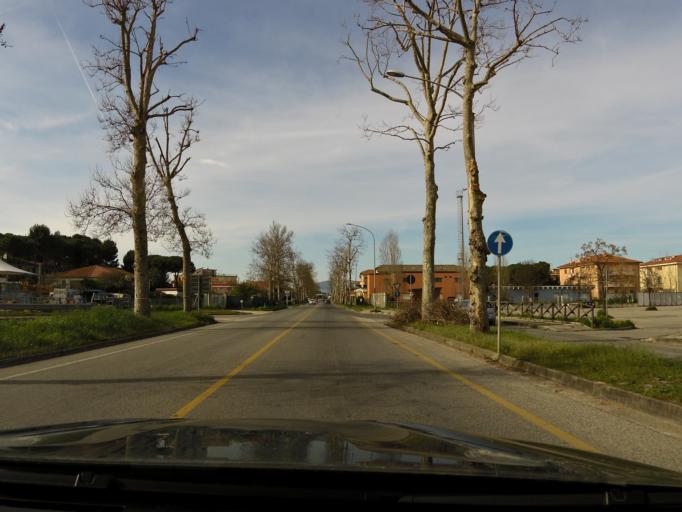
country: IT
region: The Marches
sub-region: Provincia di Macerata
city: Porto Recanati
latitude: 43.4318
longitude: 13.6603
